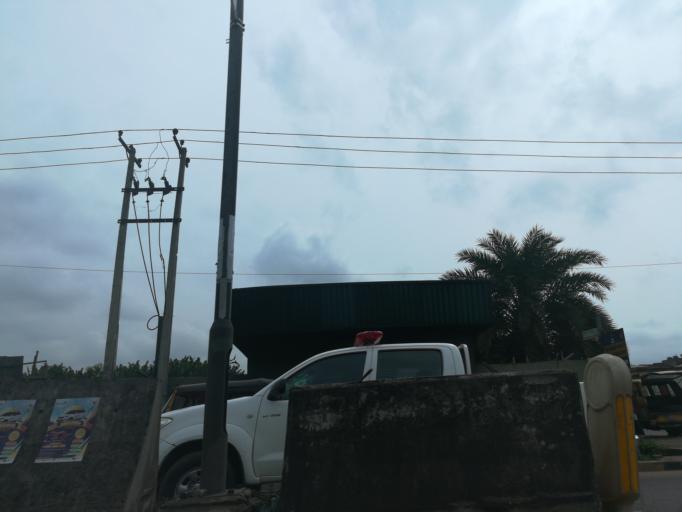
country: NG
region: Lagos
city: Ikeja
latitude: 6.6030
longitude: 3.3626
